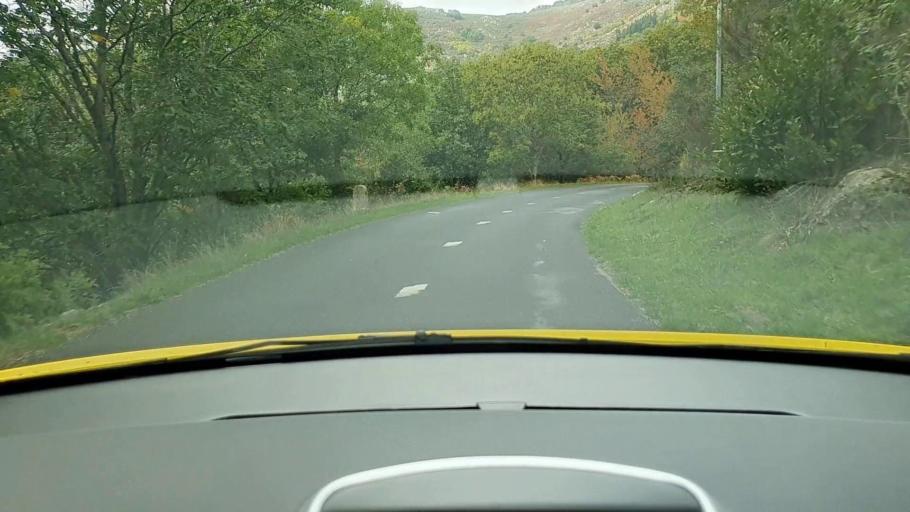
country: FR
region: Languedoc-Roussillon
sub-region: Departement de la Lozere
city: Meyrueis
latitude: 44.0684
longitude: 3.4570
